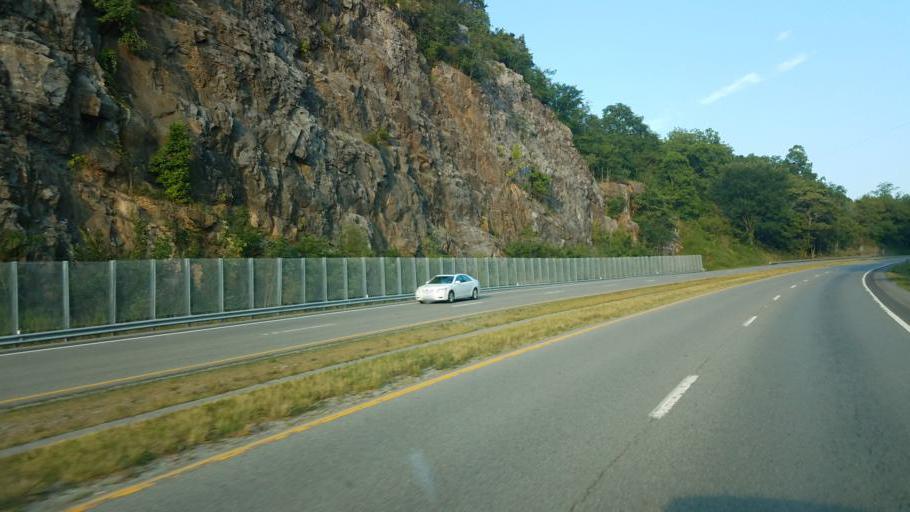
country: US
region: Virginia
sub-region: Lee County
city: Dryden
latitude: 36.7110
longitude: -82.7812
